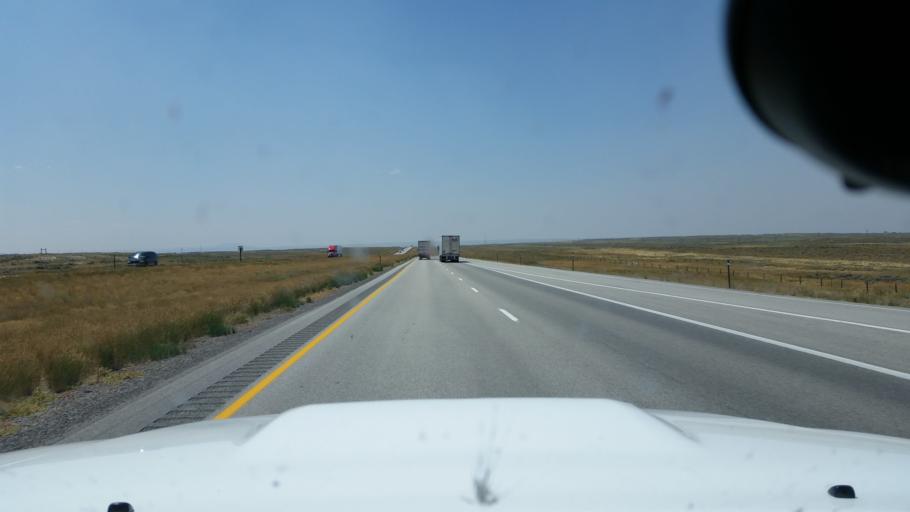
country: US
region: Wyoming
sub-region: Sweetwater County
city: Rock Springs
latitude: 41.6307
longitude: -108.3127
